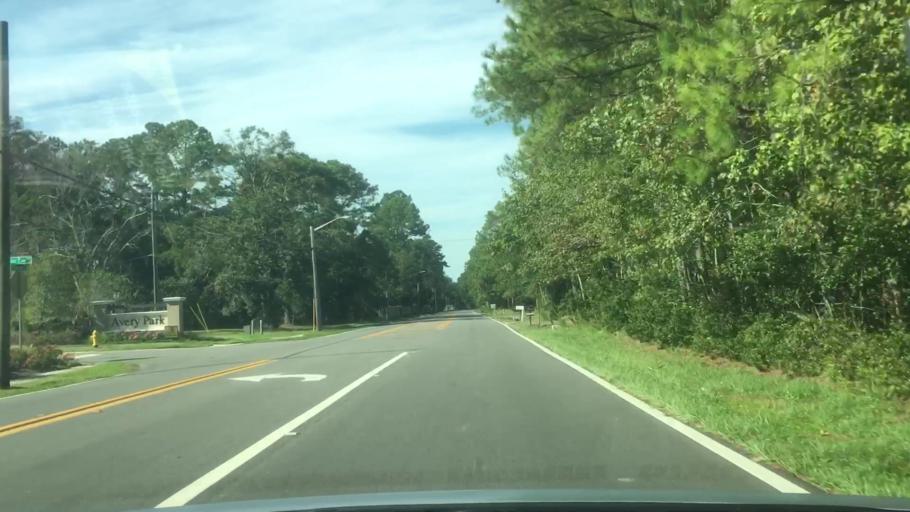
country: US
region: Florida
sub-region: Nassau County
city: Yulee
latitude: 30.4842
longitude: -81.5963
